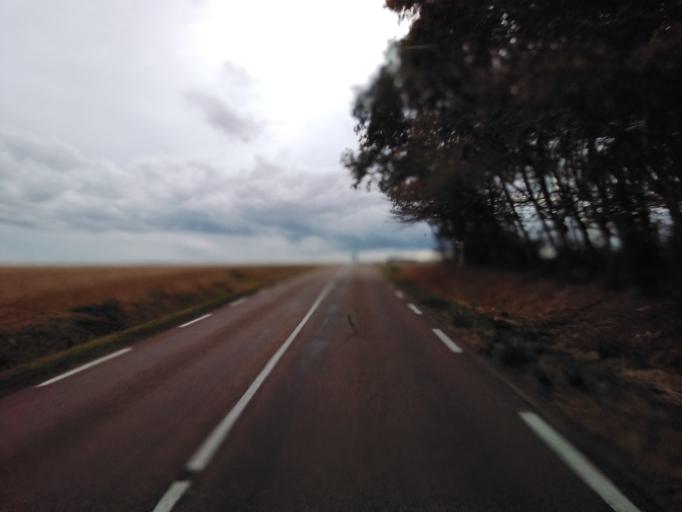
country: FR
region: Champagne-Ardenne
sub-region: Departement de l'Aube
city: Bar-sur-Seine
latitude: 48.1494
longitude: 4.4065
